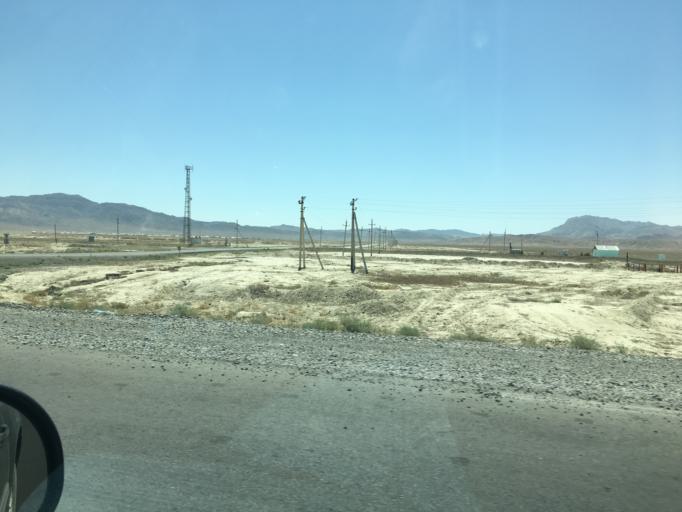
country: TM
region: Balkan
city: Serdar
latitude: 39.1062
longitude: 55.9318
